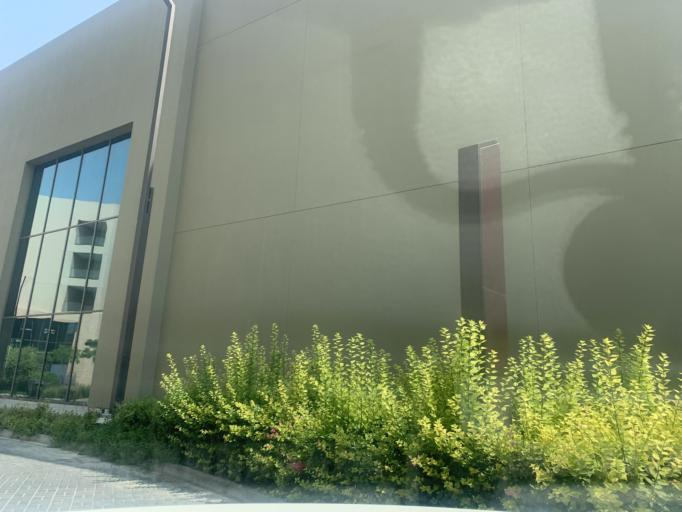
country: BH
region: Central Governorate
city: Madinat Hamad
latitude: 26.1630
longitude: 50.4702
